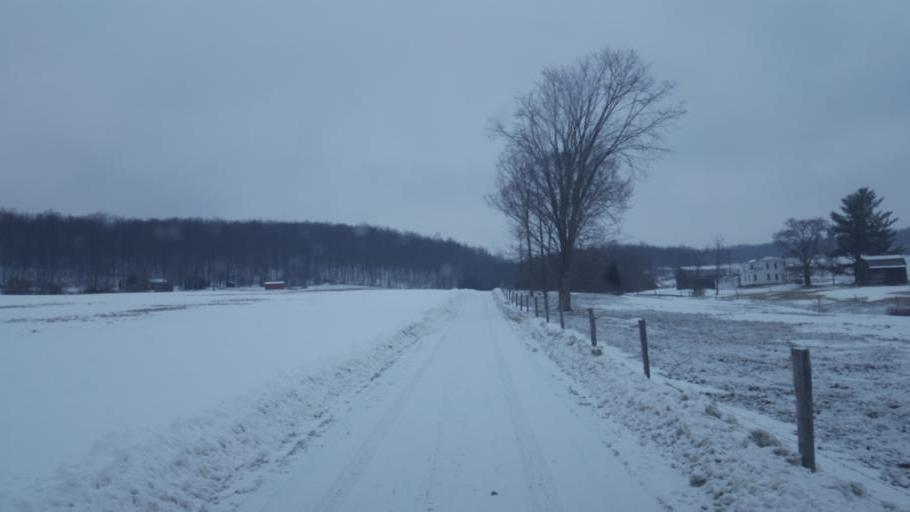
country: US
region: Pennsylvania
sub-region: Tioga County
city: Elkland
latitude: 42.0796
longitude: -77.4521
